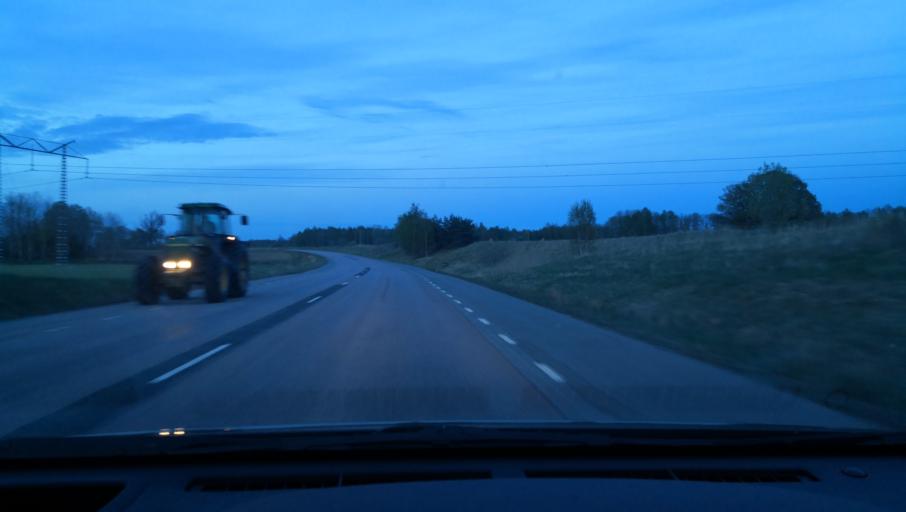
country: SE
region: OErebro
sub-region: Lekebergs Kommun
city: Fjugesta
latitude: 59.0389
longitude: 14.9119
